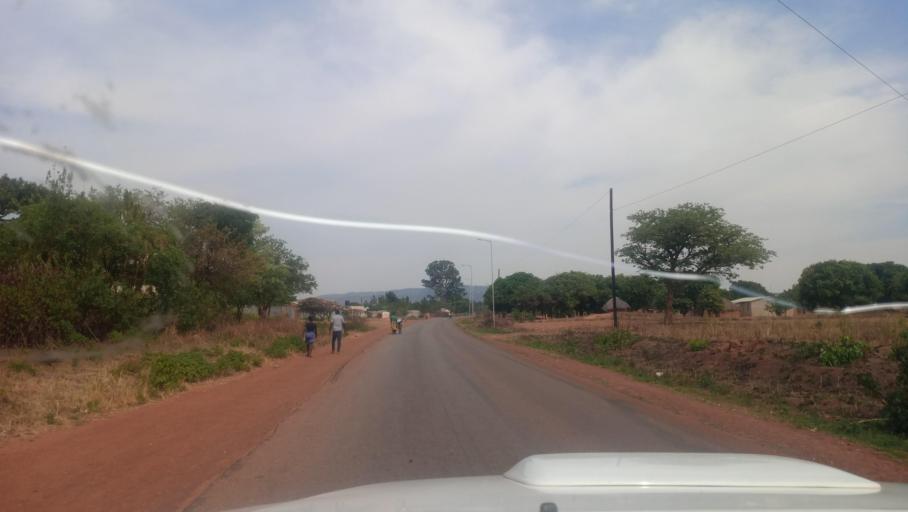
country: ZM
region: Northern
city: Mpika
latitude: -11.8330
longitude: 31.4215
